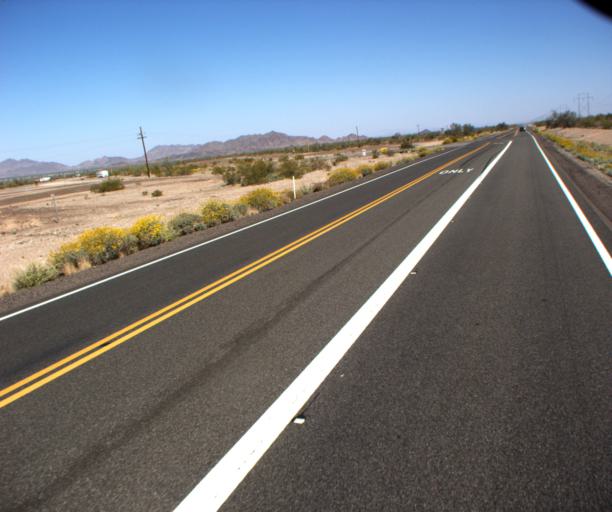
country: US
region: Arizona
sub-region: La Paz County
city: Quartzsite
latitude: 33.5795
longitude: -114.2170
